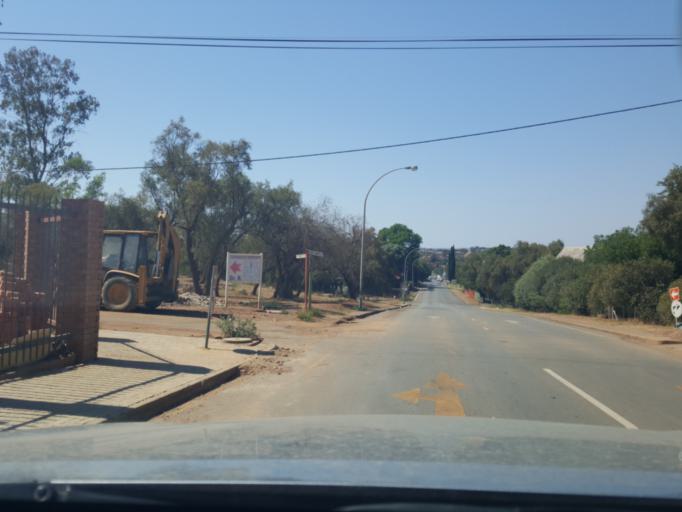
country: ZA
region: North-West
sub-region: Ngaka Modiri Molema District Municipality
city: Zeerust
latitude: -25.5398
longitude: 26.0786
